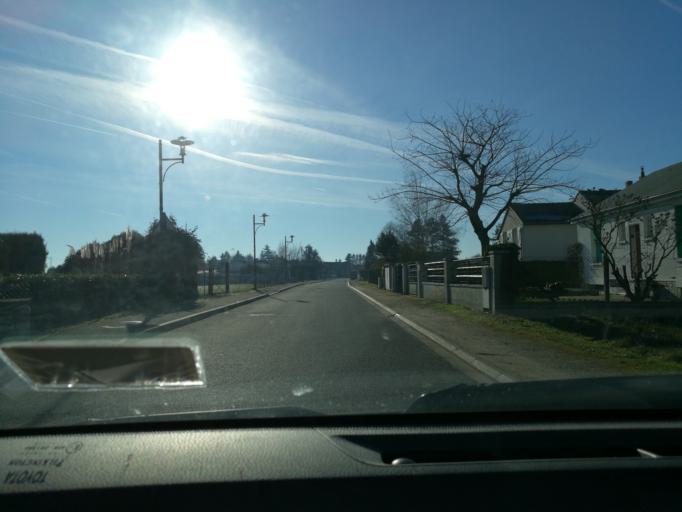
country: FR
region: Centre
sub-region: Departement du Loiret
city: Chaingy
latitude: 47.8809
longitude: 1.7645
